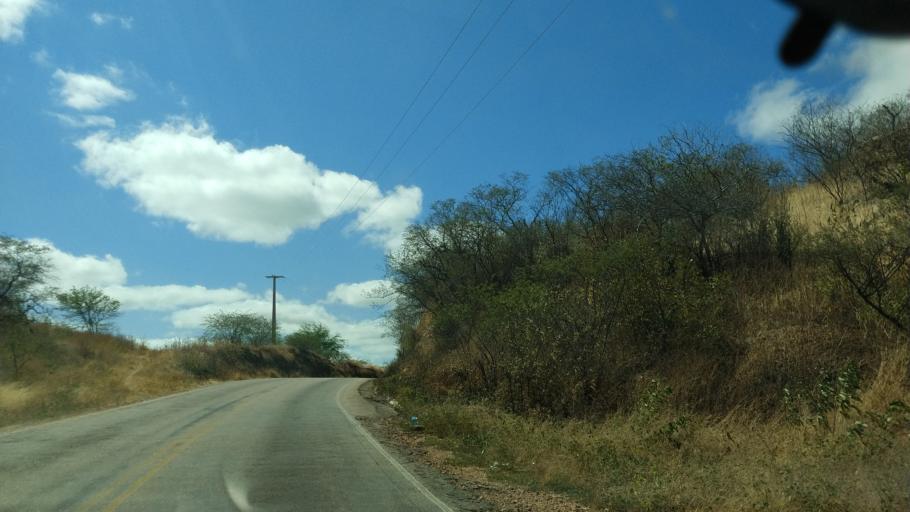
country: BR
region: Rio Grande do Norte
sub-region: Currais Novos
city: Currais Novos
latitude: -6.2626
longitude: -36.5970
